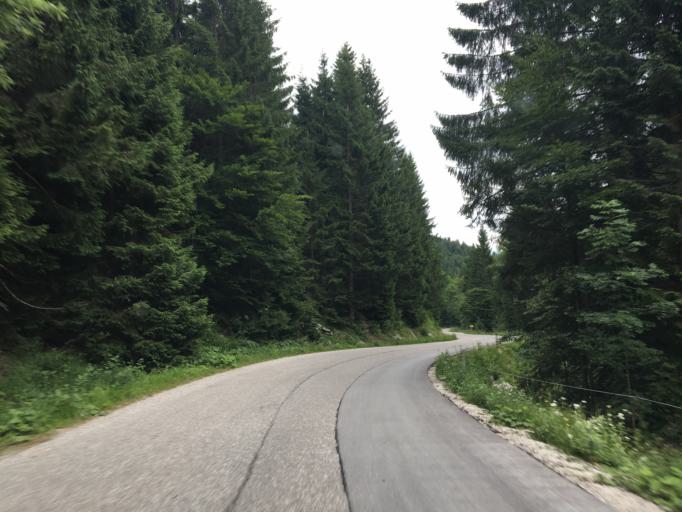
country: AT
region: Salzburg
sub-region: Politischer Bezirk Salzburg-Umgebung
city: Strobl
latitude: 47.6587
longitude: 13.4416
